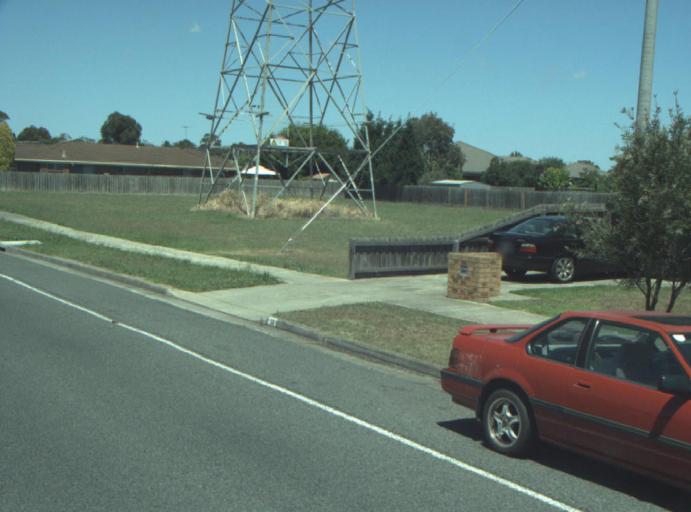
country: AU
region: Victoria
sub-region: Greater Geelong
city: Wandana Heights
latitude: -38.1969
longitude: 144.3331
